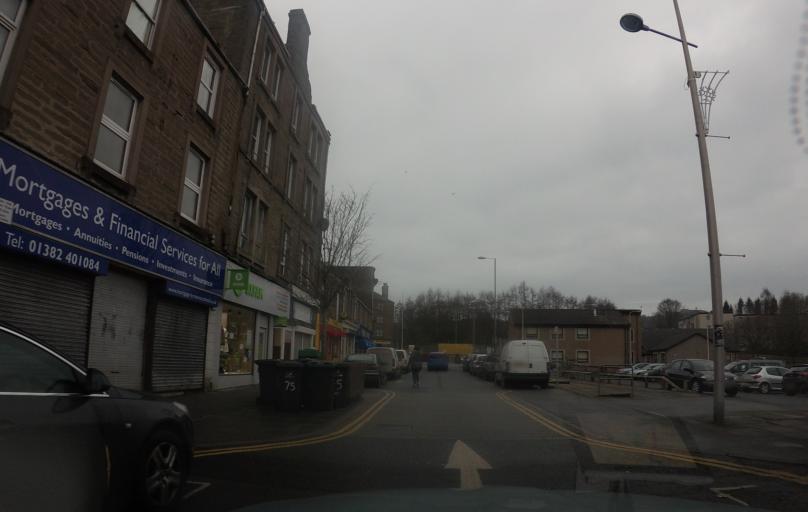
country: GB
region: Scotland
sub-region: Dundee City
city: Dundee
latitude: 56.4714
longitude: -3.0096
